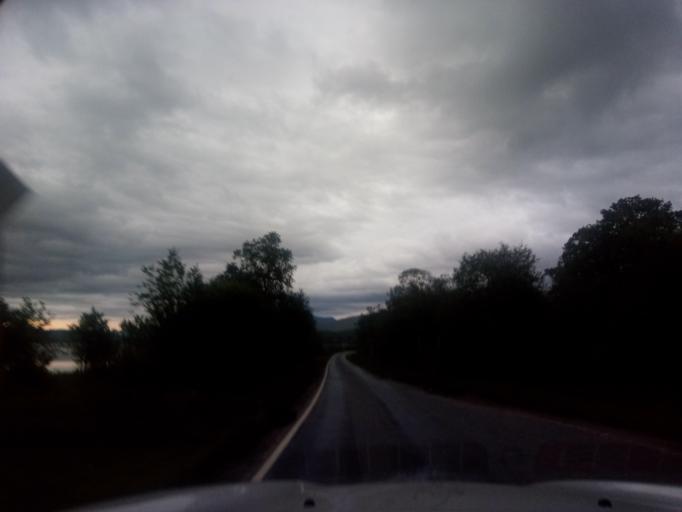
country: GB
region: Scotland
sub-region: Highland
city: Fort William
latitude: 56.8519
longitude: -5.3276
